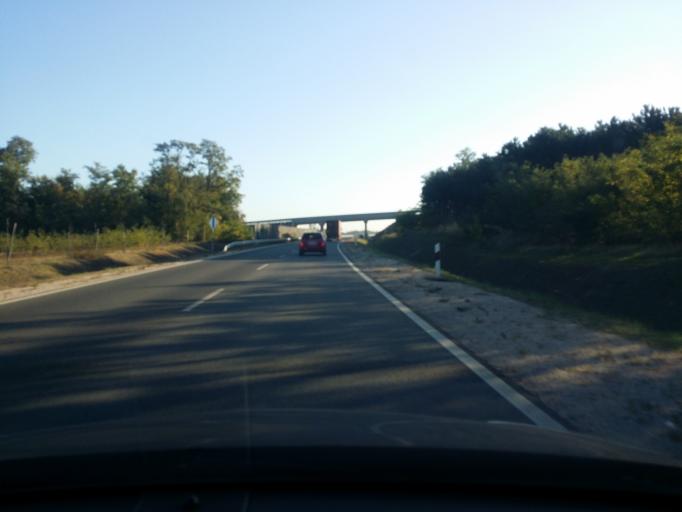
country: HU
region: Bacs-Kiskun
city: Kecskemet
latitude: 46.9476
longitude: 19.6686
